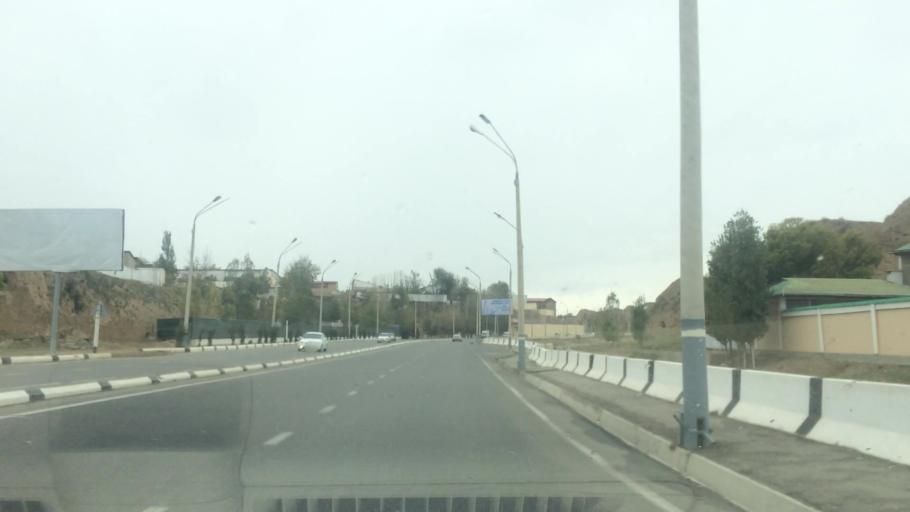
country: UZ
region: Samarqand
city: Samarqand
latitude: 39.6702
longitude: 66.9995
